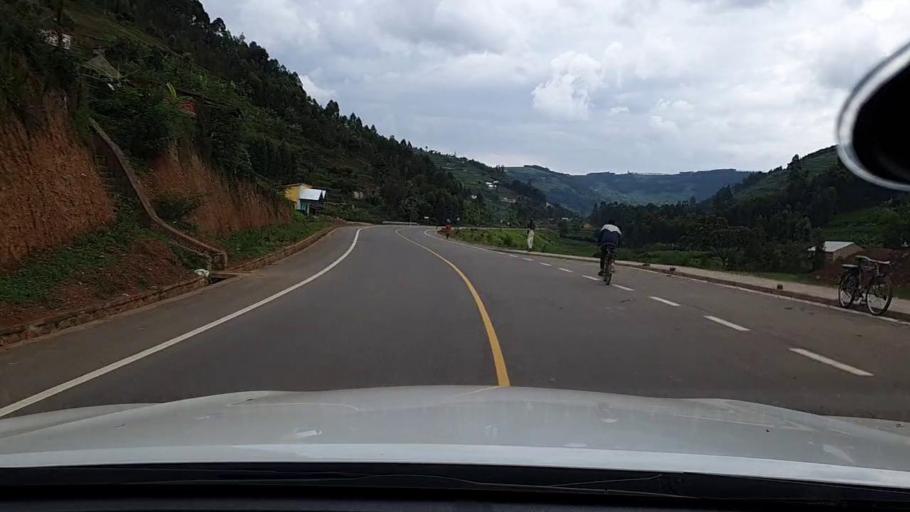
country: RW
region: Northern Province
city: Byumba
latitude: -1.6345
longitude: 29.9281
